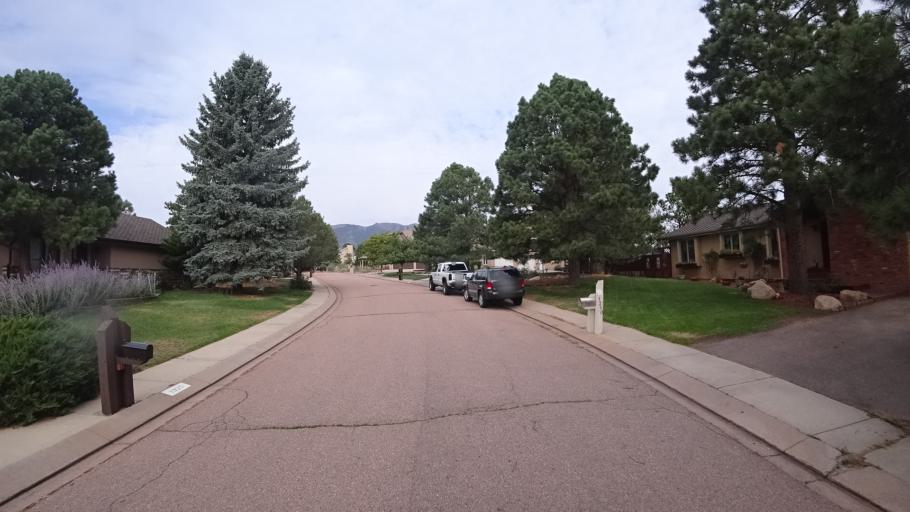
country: US
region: Colorado
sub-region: El Paso County
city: Air Force Academy
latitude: 38.9365
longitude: -104.8515
